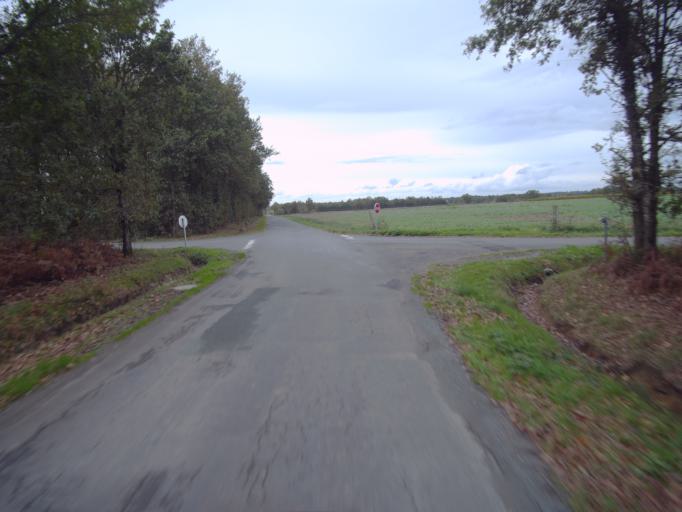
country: FR
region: Pays de la Loire
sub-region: Departement de la Loire-Atlantique
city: Remouille
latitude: 47.0397
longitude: -1.4058
